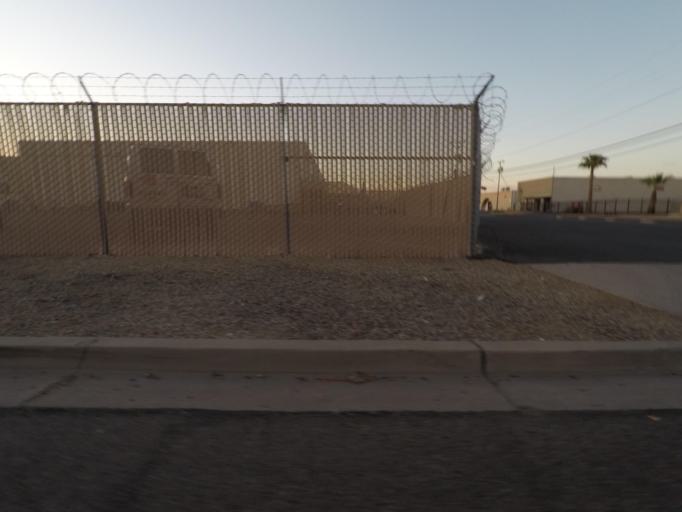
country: US
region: Arizona
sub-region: Maricopa County
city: Phoenix
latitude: 33.4897
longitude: -112.1324
